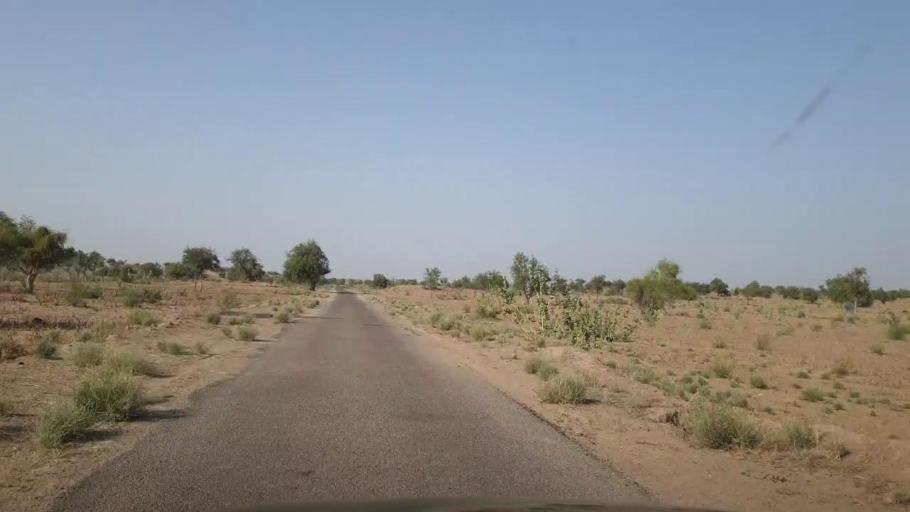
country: PK
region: Sindh
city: Islamkot
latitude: 25.1403
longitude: 70.5185
